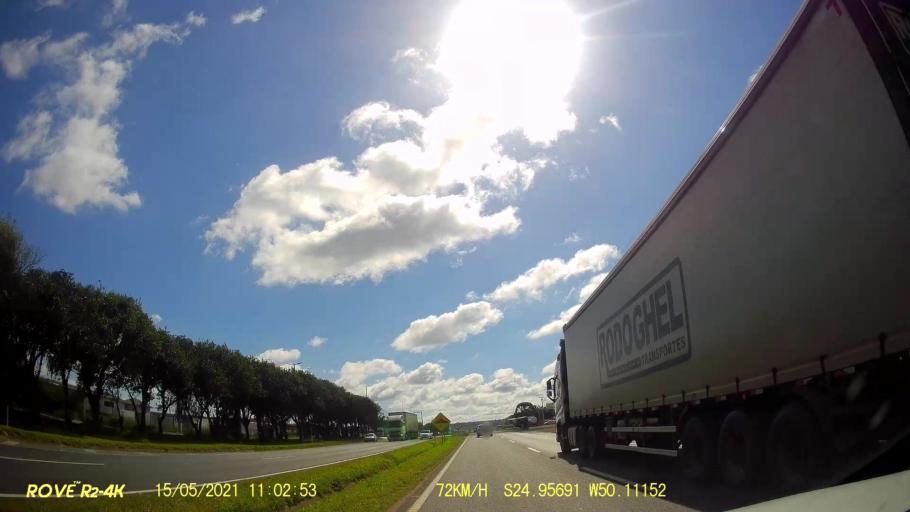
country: BR
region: Parana
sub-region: Carambei
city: Carambei
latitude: -24.9571
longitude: -50.1116
